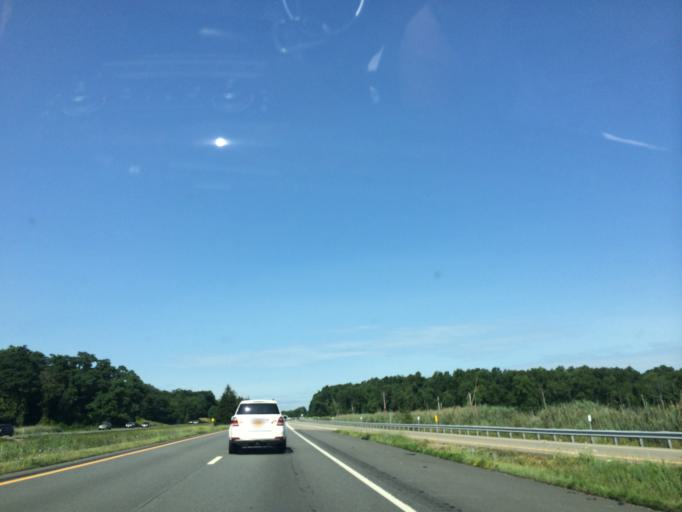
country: US
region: New York
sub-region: Orange County
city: Orange Lake
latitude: 41.5125
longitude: -74.1334
